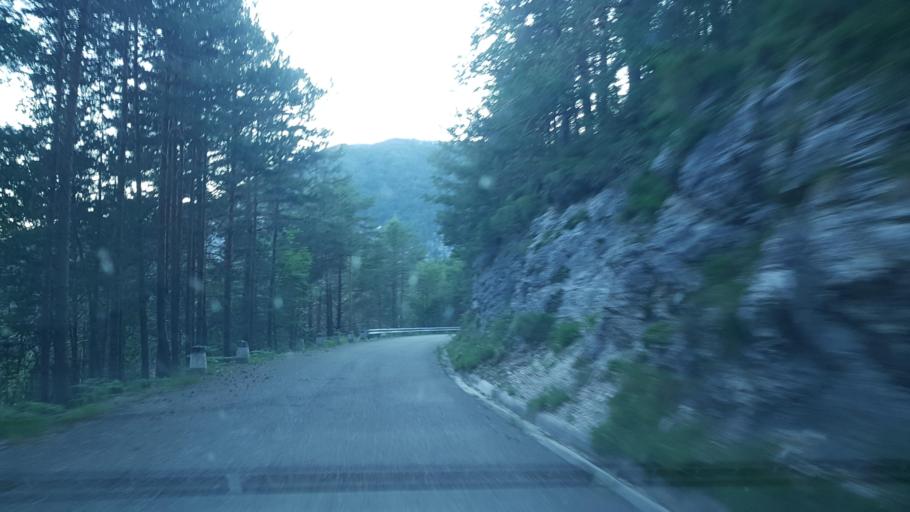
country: IT
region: Friuli Venezia Giulia
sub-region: Provincia di Udine
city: Malborghetto
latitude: 46.4597
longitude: 13.3857
